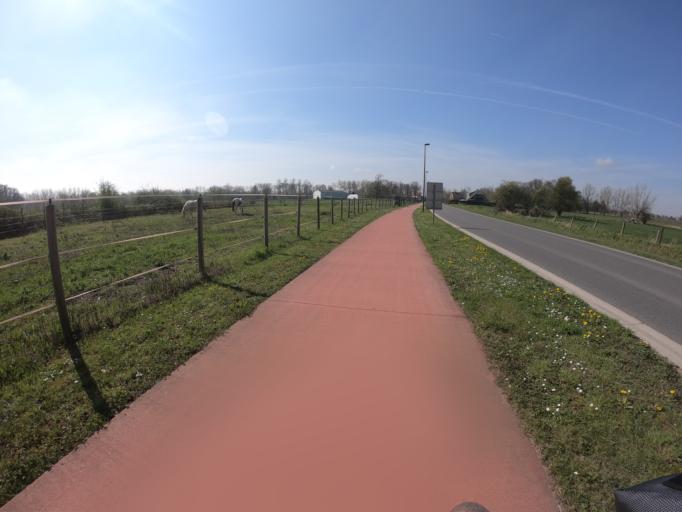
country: BE
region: Flanders
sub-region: Provincie Vlaams-Brabant
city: Geetbets
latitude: 50.9003
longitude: 5.1193
